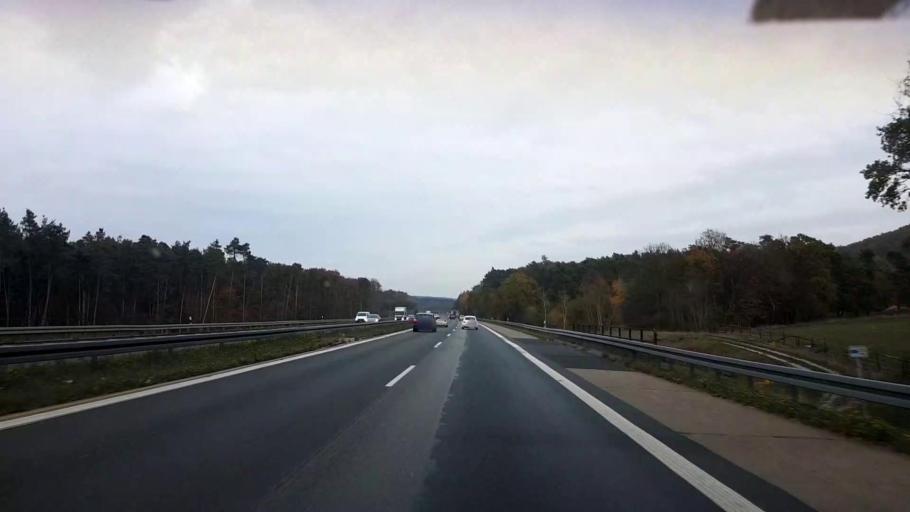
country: DE
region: Bavaria
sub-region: Regierungsbezirk Unterfranken
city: Wiesentheid
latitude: 49.7781
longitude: 10.4002
